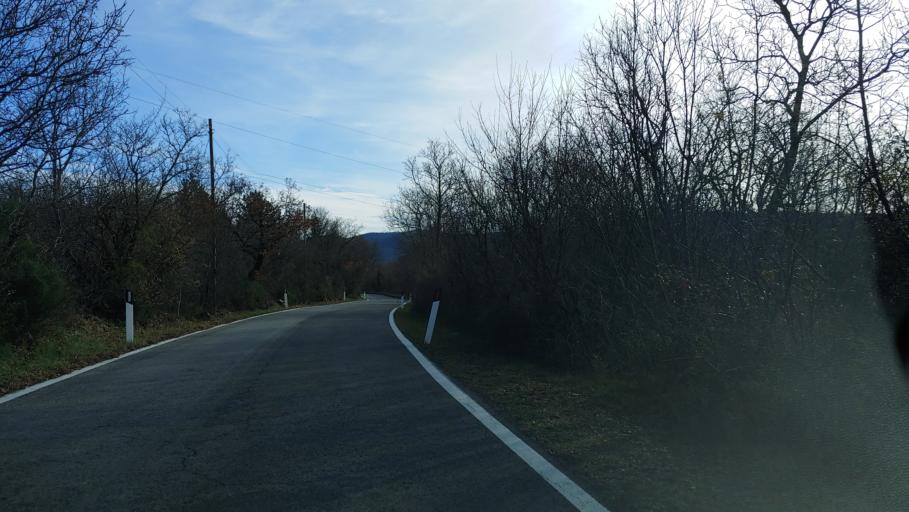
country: IT
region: Friuli Venezia Giulia
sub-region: Provincia di Trieste
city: Duino
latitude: 45.8189
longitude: 13.5863
